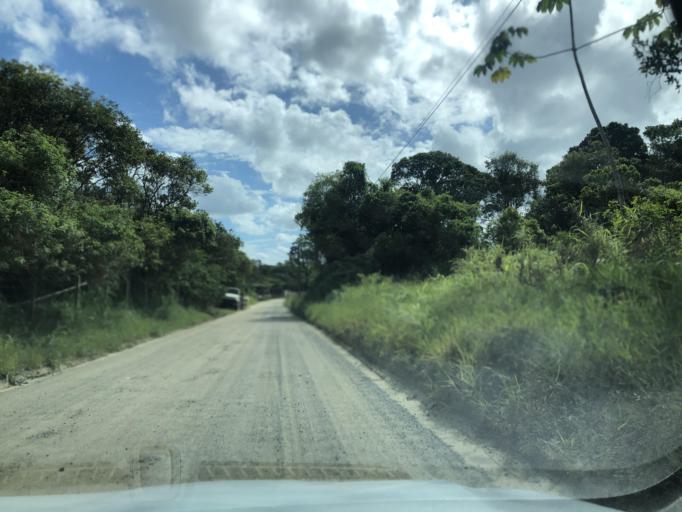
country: BR
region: Santa Catarina
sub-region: Sao Francisco Do Sul
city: Sao Francisco do Sul
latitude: -26.2249
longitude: -48.5789
